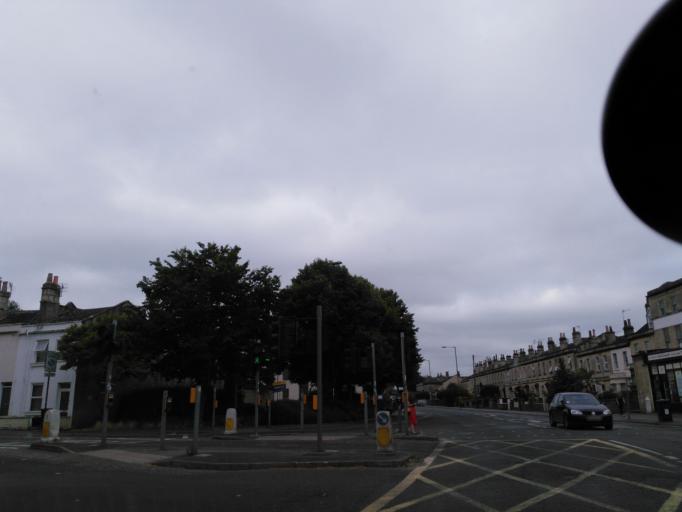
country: GB
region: England
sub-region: Bath and North East Somerset
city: Bath
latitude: 51.3811
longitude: -2.3741
